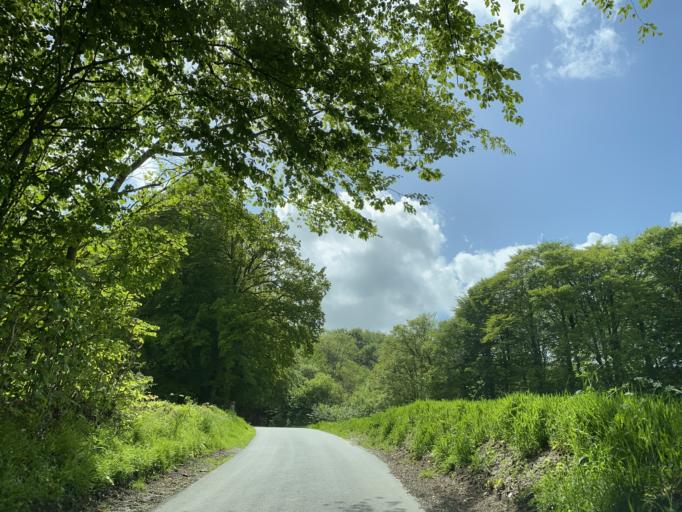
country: DK
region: South Denmark
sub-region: Aabenraa Kommune
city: Aabenraa
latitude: 55.0052
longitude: 9.4694
